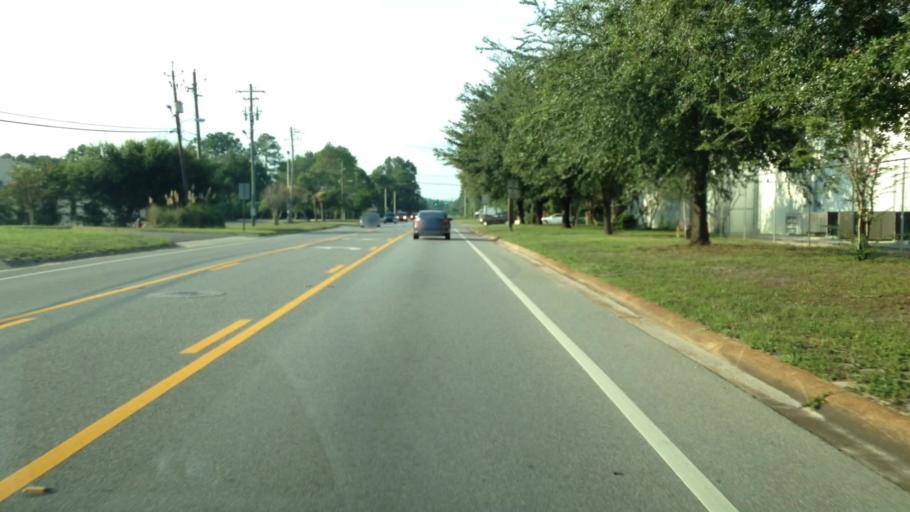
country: US
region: Florida
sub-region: Okaloosa County
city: Mary Esther
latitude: 30.4216
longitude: -86.6673
